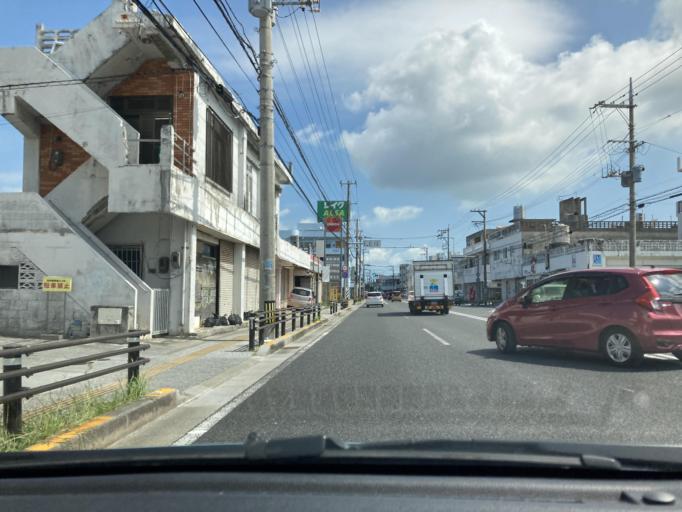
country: JP
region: Okinawa
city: Ginowan
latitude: 26.2759
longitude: 127.7759
